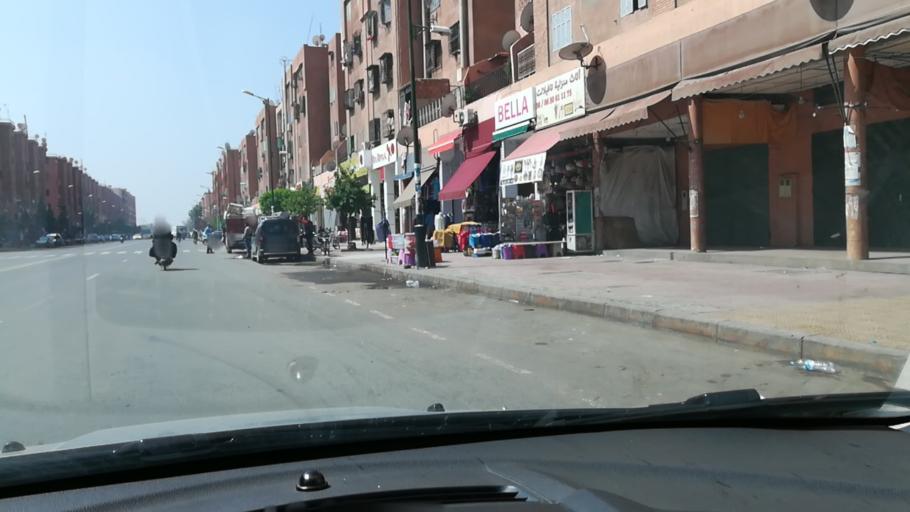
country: MA
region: Marrakech-Tensift-Al Haouz
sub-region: Marrakech
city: Marrakesh
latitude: 31.6328
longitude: -8.0584
